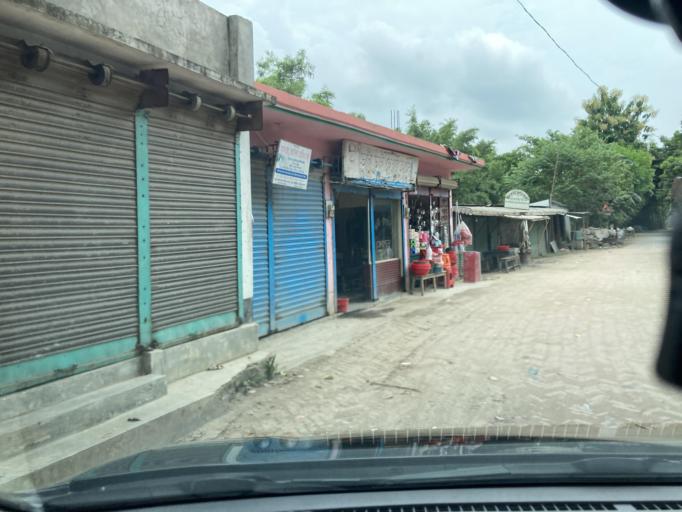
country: BD
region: Dhaka
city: Dohar
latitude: 23.7809
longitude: 90.0667
